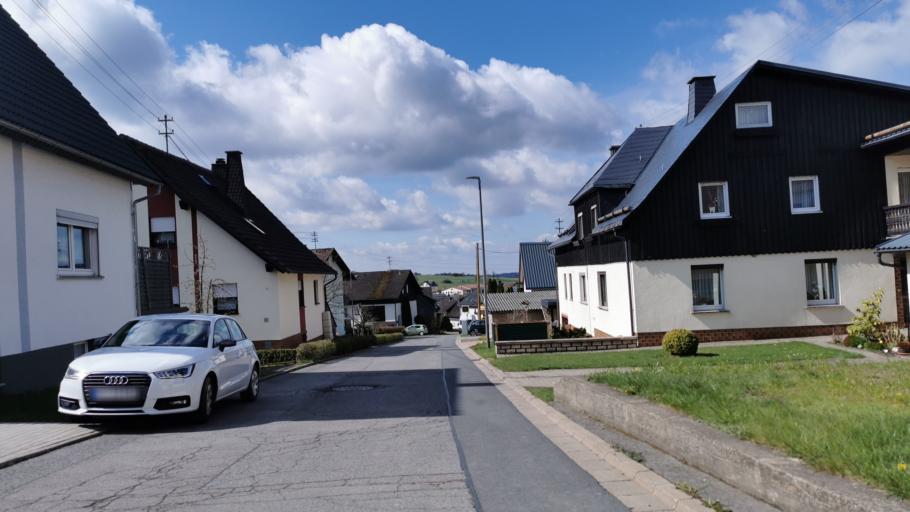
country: DE
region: Bavaria
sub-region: Upper Franconia
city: Teuschnitz
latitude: 50.4184
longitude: 11.3384
